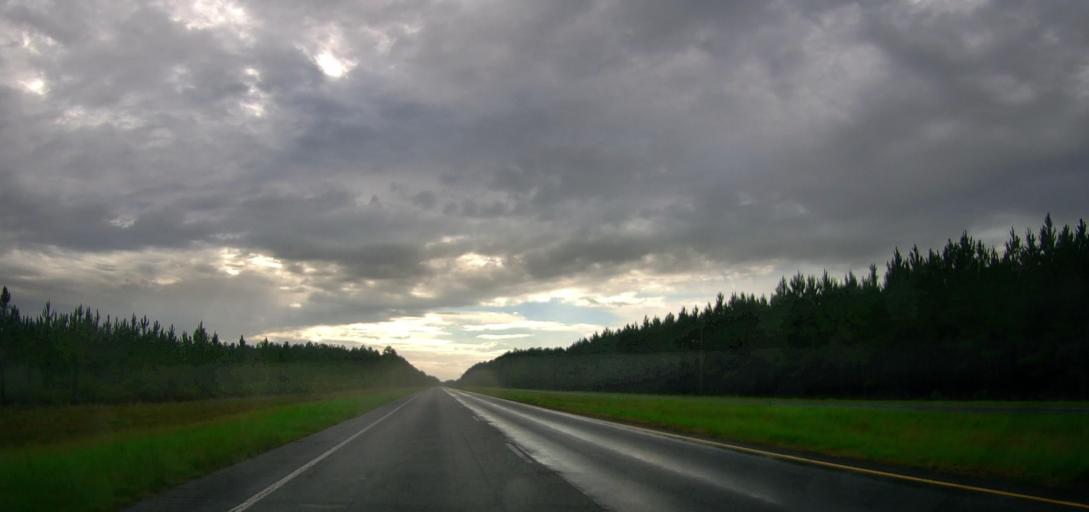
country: US
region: Georgia
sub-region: Ware County
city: Deenwood
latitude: 31.2584
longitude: -82.5011
